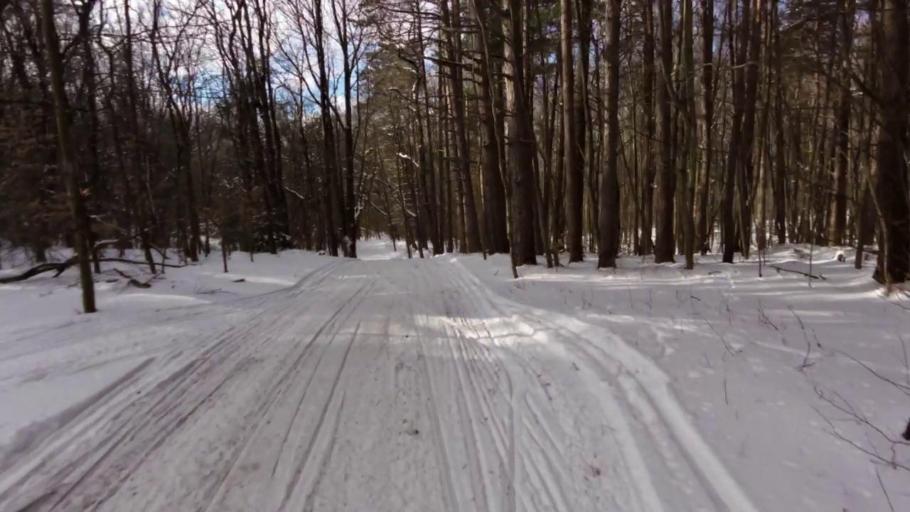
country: US
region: Pennsylvania
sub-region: McKean County
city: Bradford
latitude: 42.0273
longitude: -78.7139
